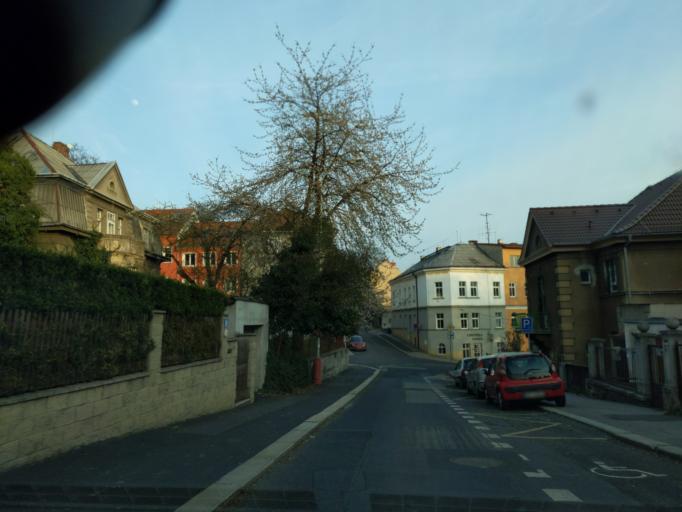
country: CZ
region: Ustecky
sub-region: Okres Usti nad Labem
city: Usti nad Labem
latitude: 50.6681
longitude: 14.0296
